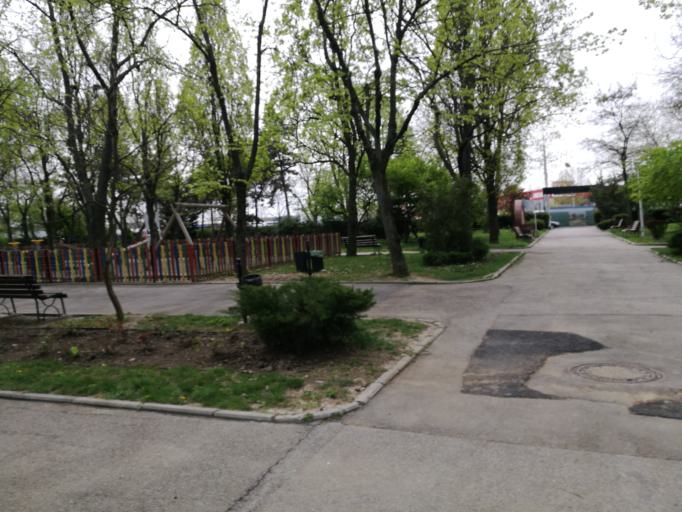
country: RO
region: Ilfov
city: Dobroesti
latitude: 44.4411
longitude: 26.1842
